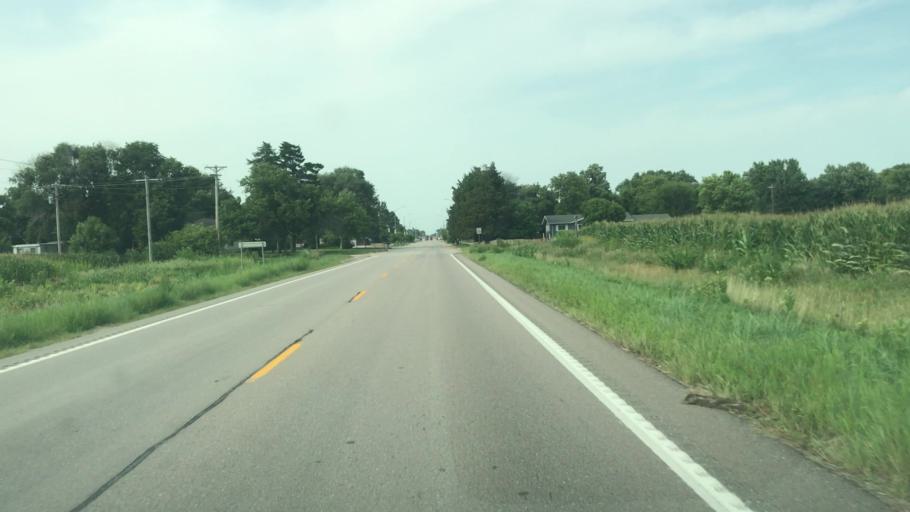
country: US
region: Nebraska
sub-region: Hall County
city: Wood River
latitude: 40.9951
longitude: -98.6075
